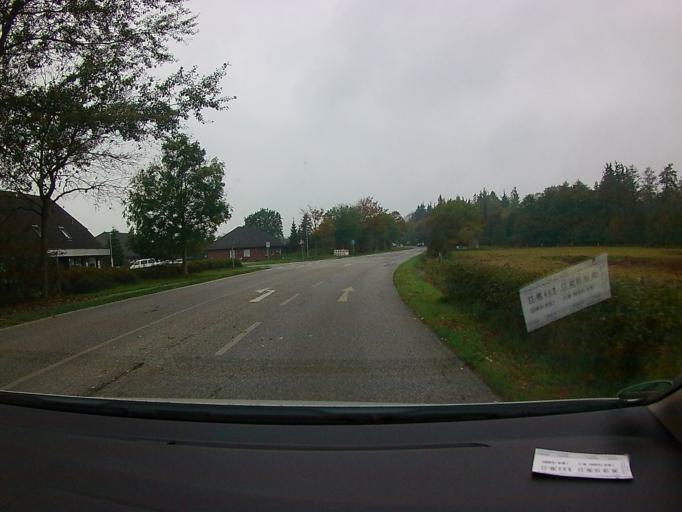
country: DE
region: Schleswig-Holstein
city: Breklum
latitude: 54.6104
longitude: 8.9838
